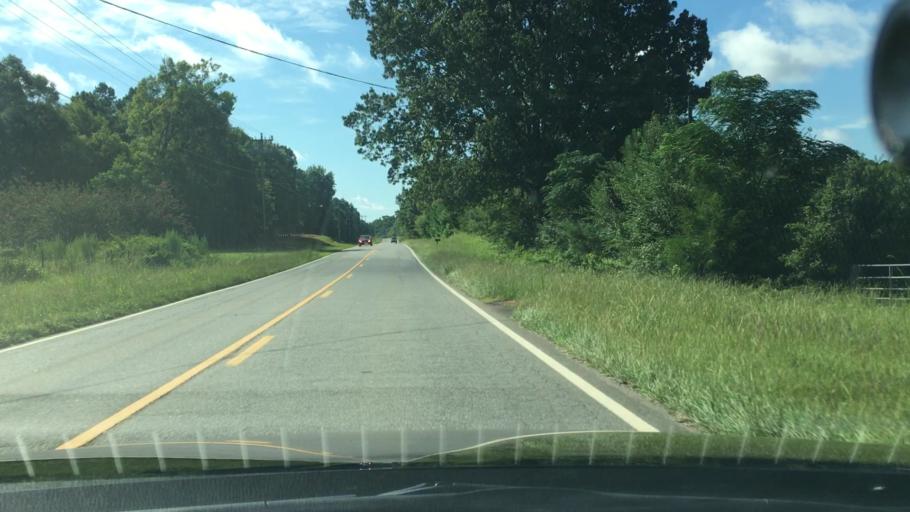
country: US
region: Georgia
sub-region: Putnam County
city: Jefferson
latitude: 33.4492
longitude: -83.2968
